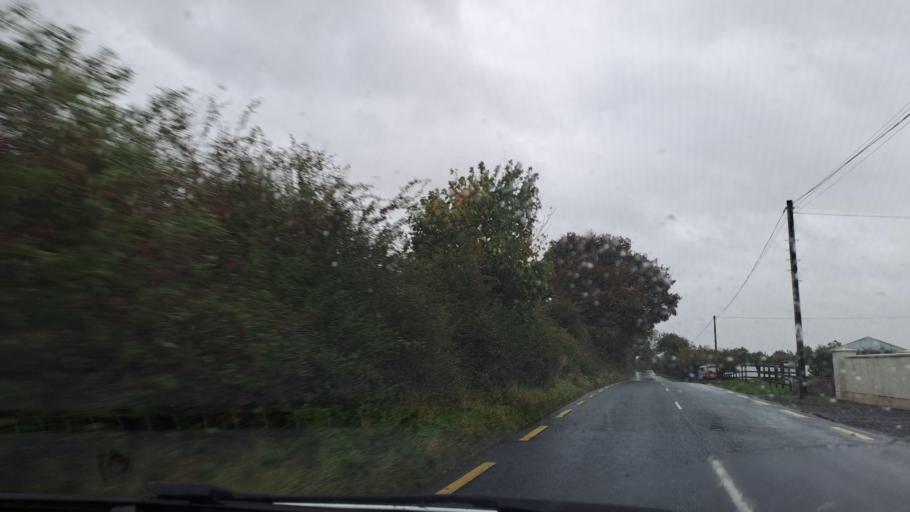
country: GB
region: Northern Ireland
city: Crossmaglen
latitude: 53.9714
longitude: -6.5944
